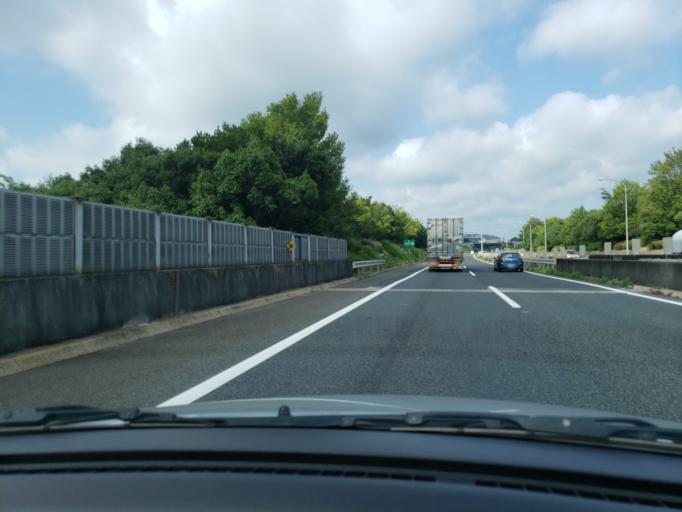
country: JP
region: Hiroshima
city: Onomichi
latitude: 34.4637
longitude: 133.2430
